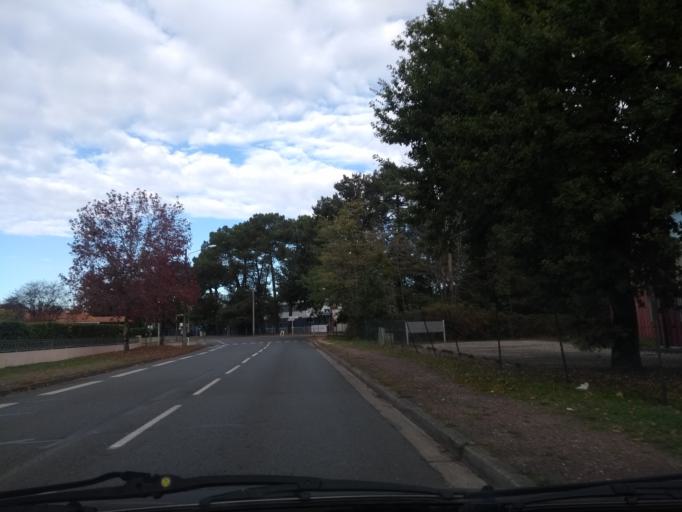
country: FR
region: Aquitaine
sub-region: Departement de la Gironde
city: Canejan
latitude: 44.7729
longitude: -0.6332
